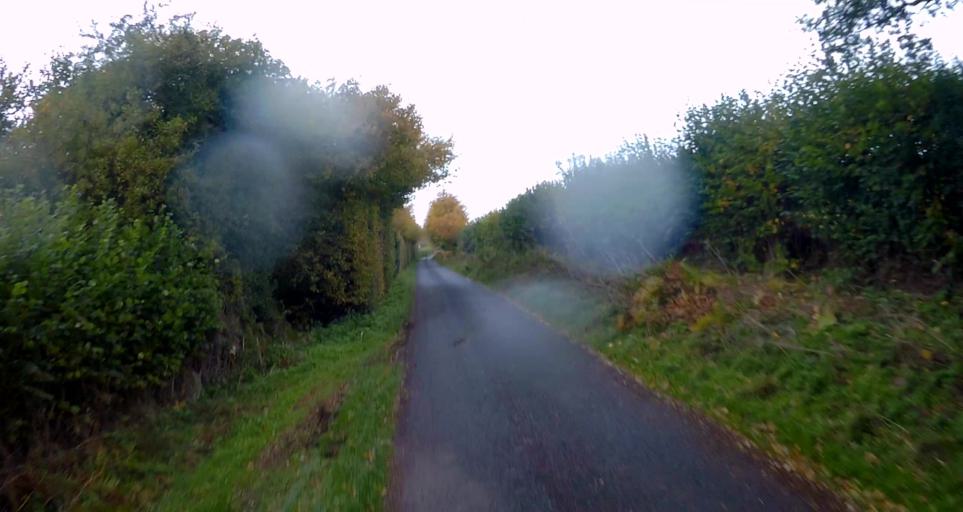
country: GB
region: England
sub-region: Hampshire
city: Four Marks
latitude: 51.1560
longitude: -1.0781
